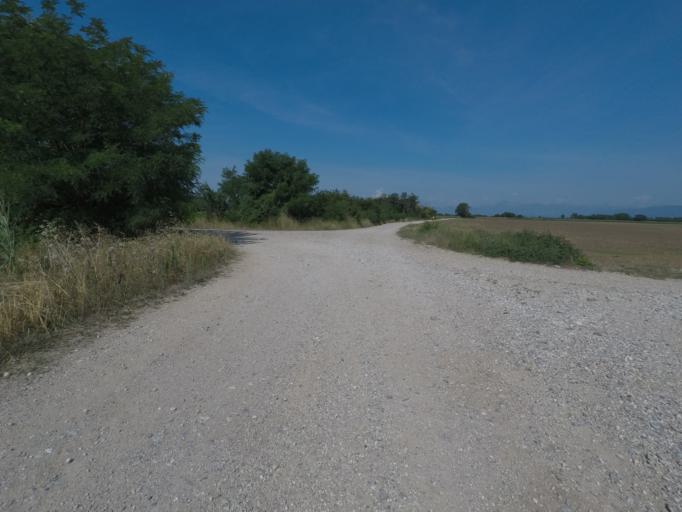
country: IT
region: Friuli Venezia Giulia
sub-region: Provincia di Udine
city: Mereto di Tomba
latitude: 46.0664
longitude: 13.0577
